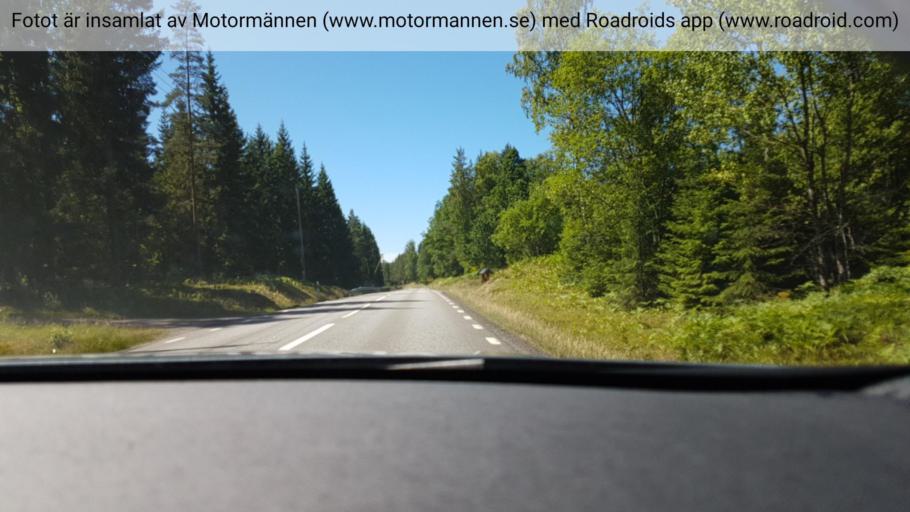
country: SE
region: Joenkoeping
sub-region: Mullsjo Kommun
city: Mullsjoe
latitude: 57.7933
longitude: 13.8402
